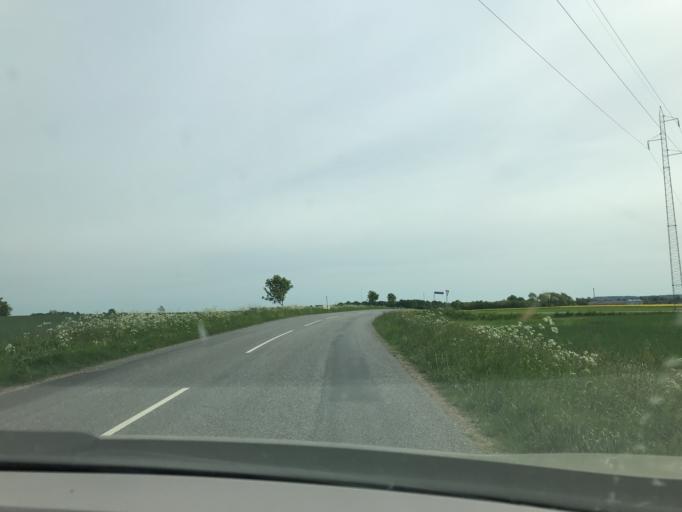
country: DK
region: Central Jutland
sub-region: Norddjurs Kommune
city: Allingabro
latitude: 56.5168
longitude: 10.3292
